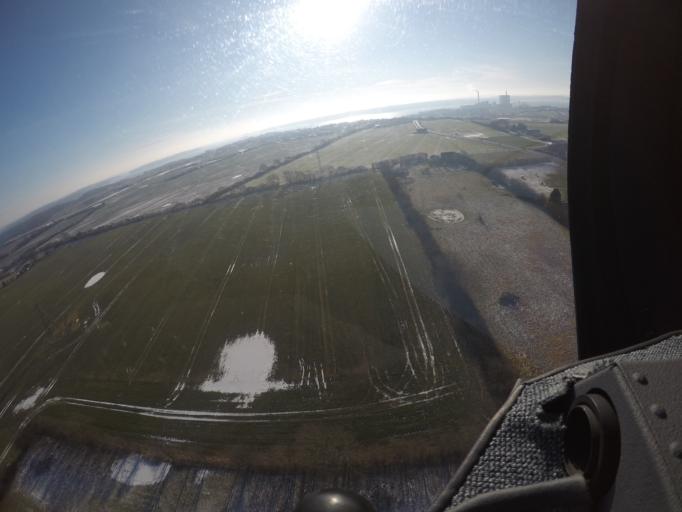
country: DK
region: South Denmark
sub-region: Fredericia Kommune
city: Taulov
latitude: 55.5309
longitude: 9.6243
